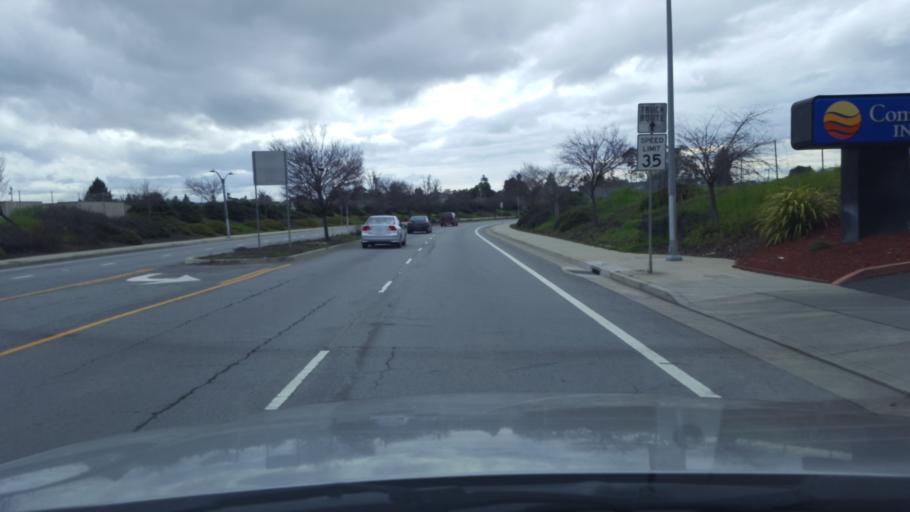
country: US
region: California
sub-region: Santa Cruz County
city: Freedom
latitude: 36.9371
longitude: -121.7789
